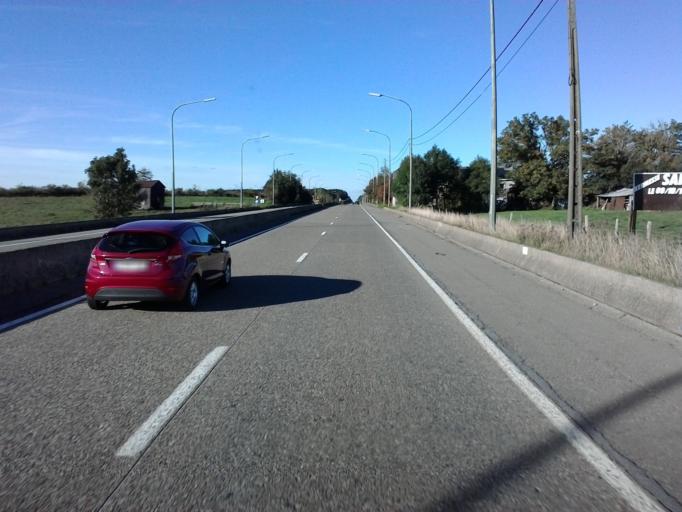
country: BE
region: Wallonia
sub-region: Province du Luxembourg
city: Bastogne
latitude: 49.9266
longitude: 5.7054
